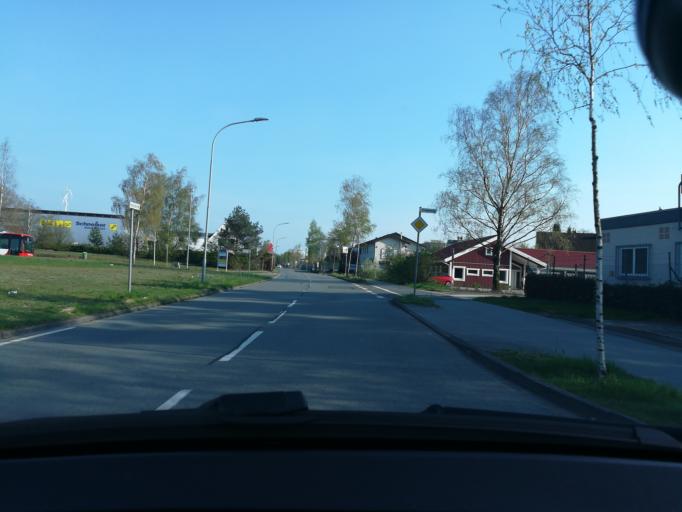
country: DE
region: North Rhine-Westphalia
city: Halle
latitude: 52.0462
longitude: 8.3763
